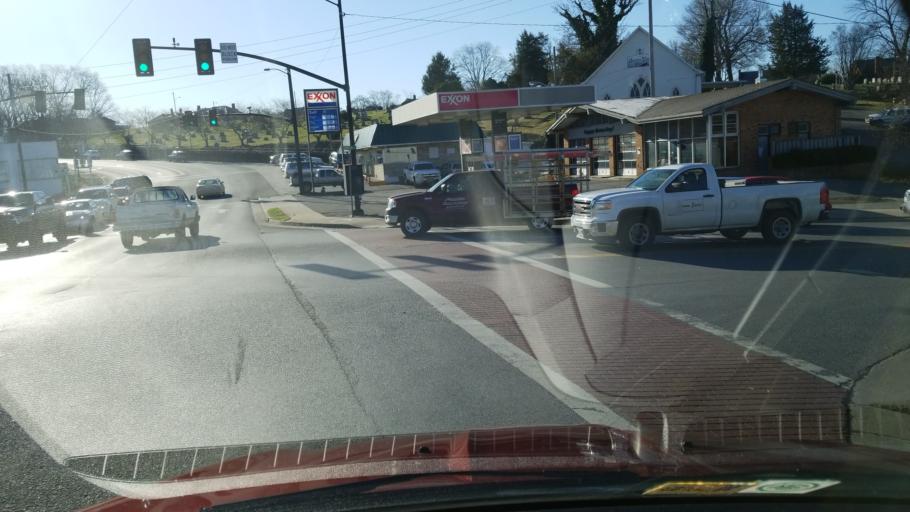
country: US
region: Virginia
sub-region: Franklin County
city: Rocky Mount
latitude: 37.0009
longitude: -79.8903
